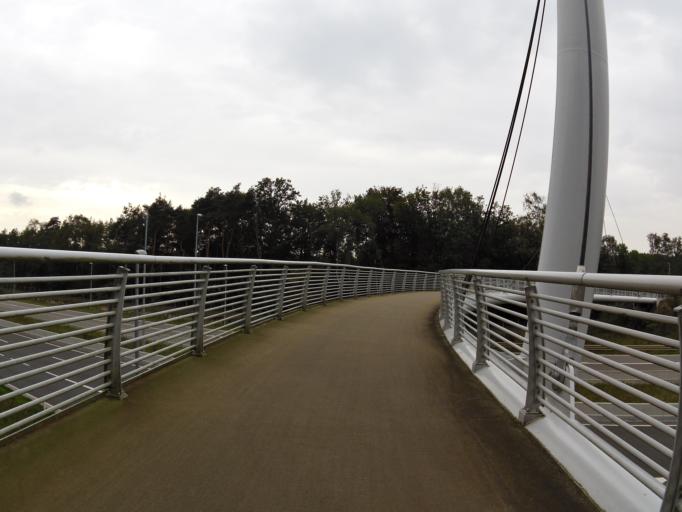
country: BE
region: Flanders
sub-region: Provincie Limburg
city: As
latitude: 51.0041
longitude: 5.6031
